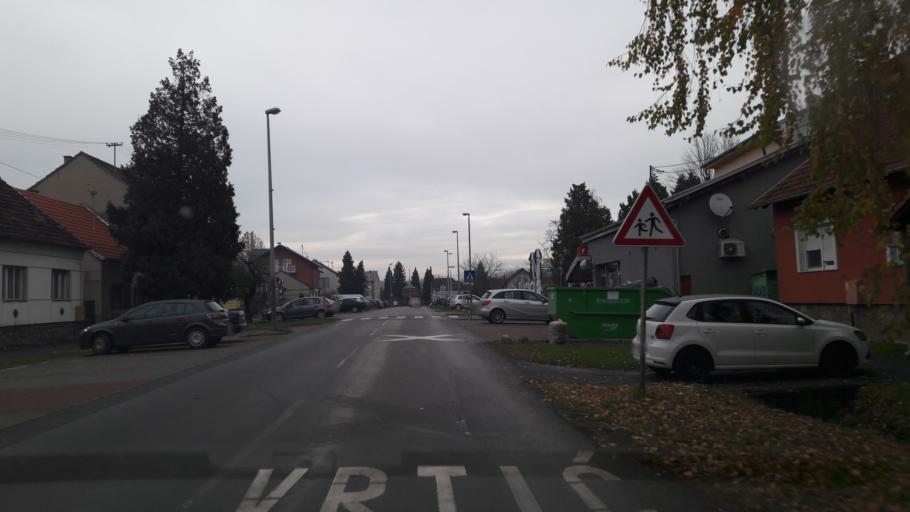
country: HR
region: Osjecko-Baranjska
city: Visnjevac
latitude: 45.5643
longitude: 18.6193
